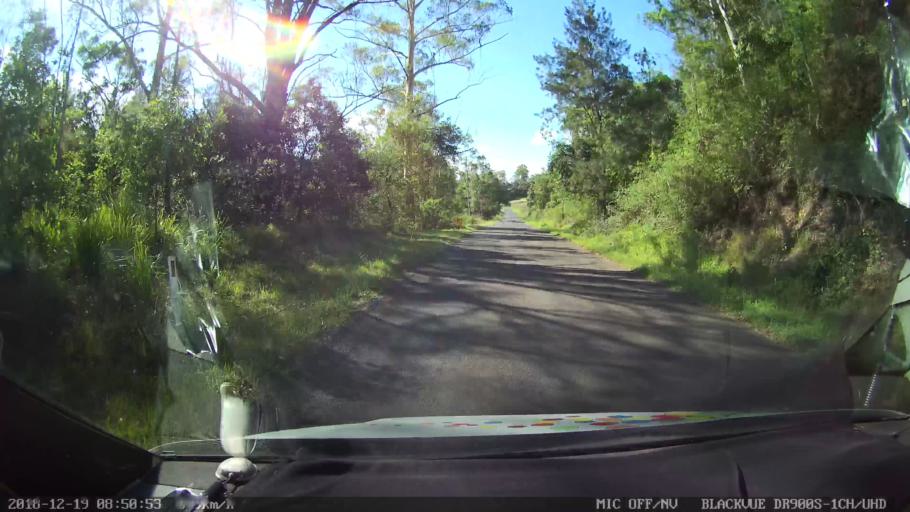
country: AU
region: New South Wales
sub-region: Kyogle
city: Kyogle
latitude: -28.3842
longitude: 152.9766
